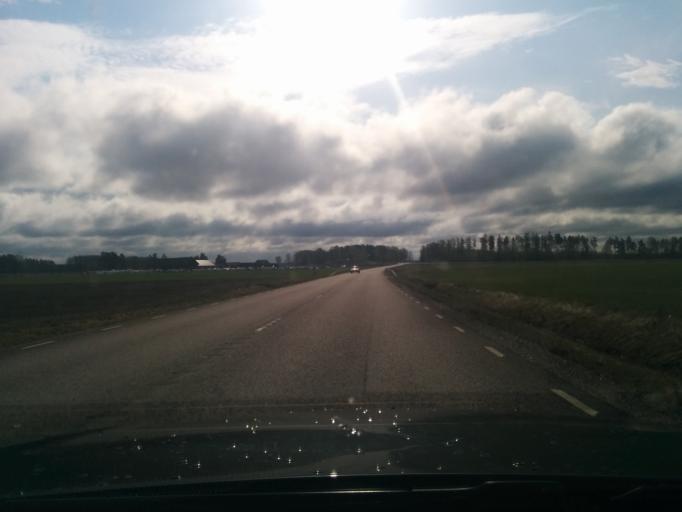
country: SE
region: Uppsala
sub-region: Tierps Kommun
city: Orbyhus
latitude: 60.1800
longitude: 17.6133
